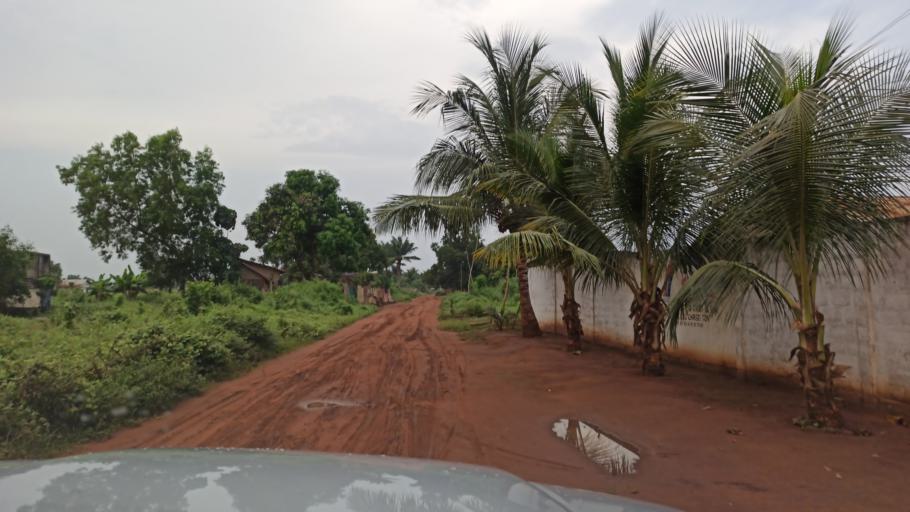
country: BJ
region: Queme
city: Porto-Novo
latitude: 6.4722
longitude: 2.6729
